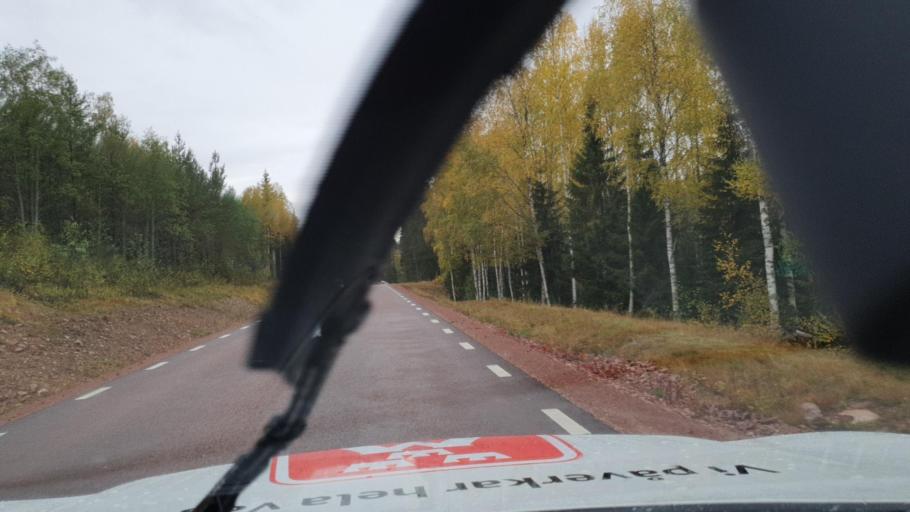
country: SE
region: Dalarna
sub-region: Alvdalens Kommun
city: AElvdalen
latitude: 61.3829
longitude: 14.0775
